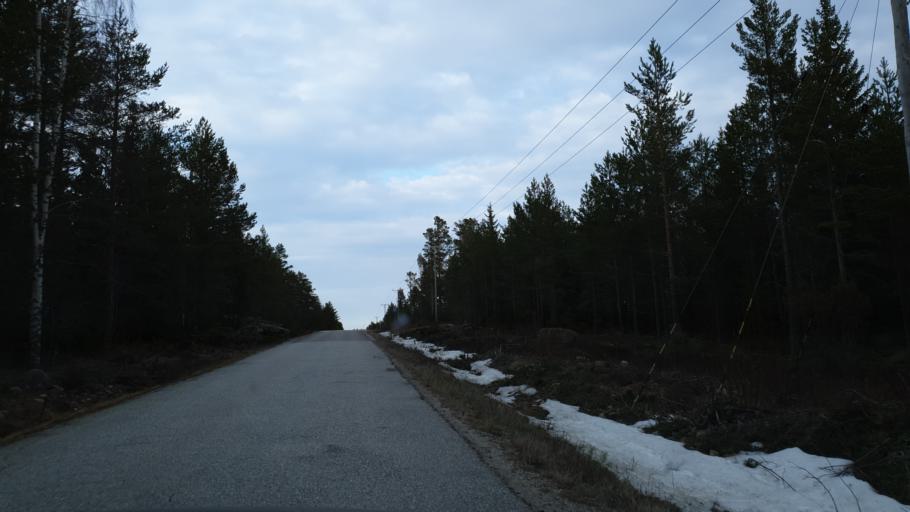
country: SE
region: Vaesternorrland
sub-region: Sundsvalls Kommun
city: Njurundabommen
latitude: 61.9903
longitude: 17.3778
